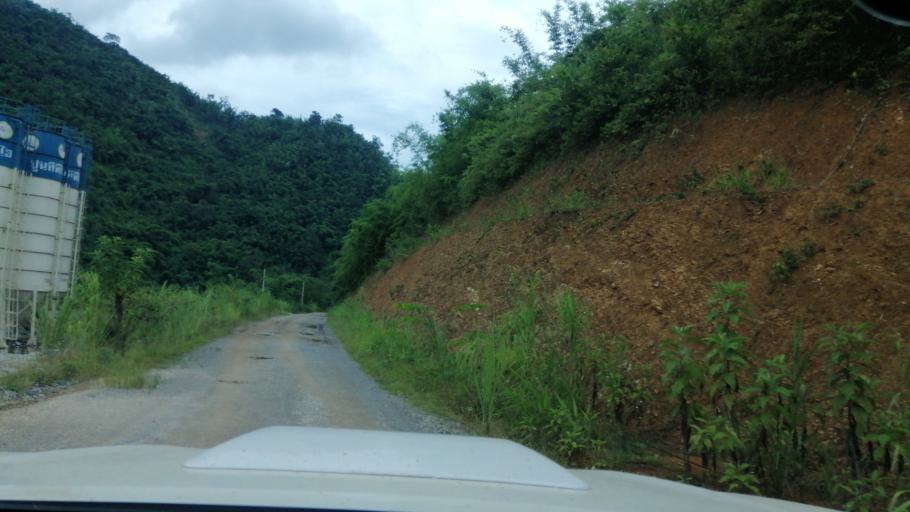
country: LA
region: Xiagnabouli
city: Sainyabuli
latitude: 19.1860
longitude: 101.7996
